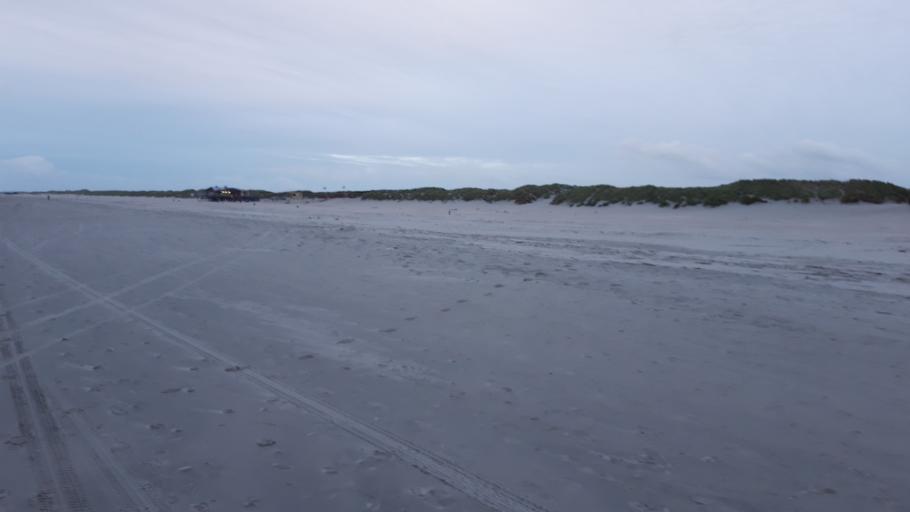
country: NL
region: Friesland
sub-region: Gemeente Ameland
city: Nes
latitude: 53.4611
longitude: 5.7719
